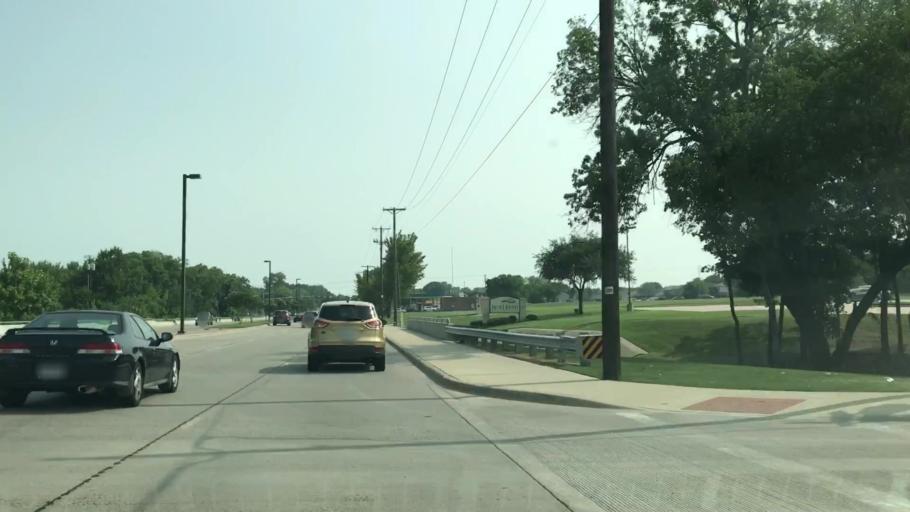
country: US
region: Texas
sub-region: Dallas County
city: Rowlett
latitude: 32.8968
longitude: -96.5697
